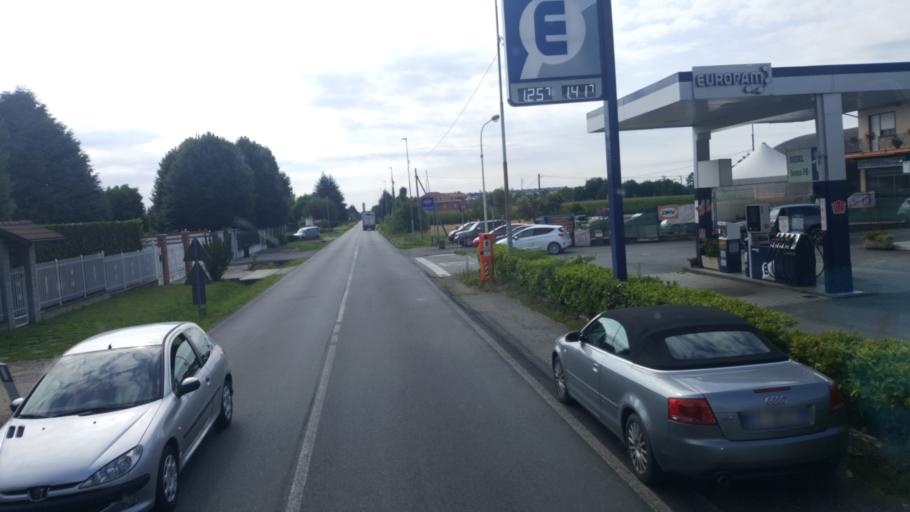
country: IT
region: Piedmont
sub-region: Provincia di Torino
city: Salassa
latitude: 45.3634
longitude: 7.6767
